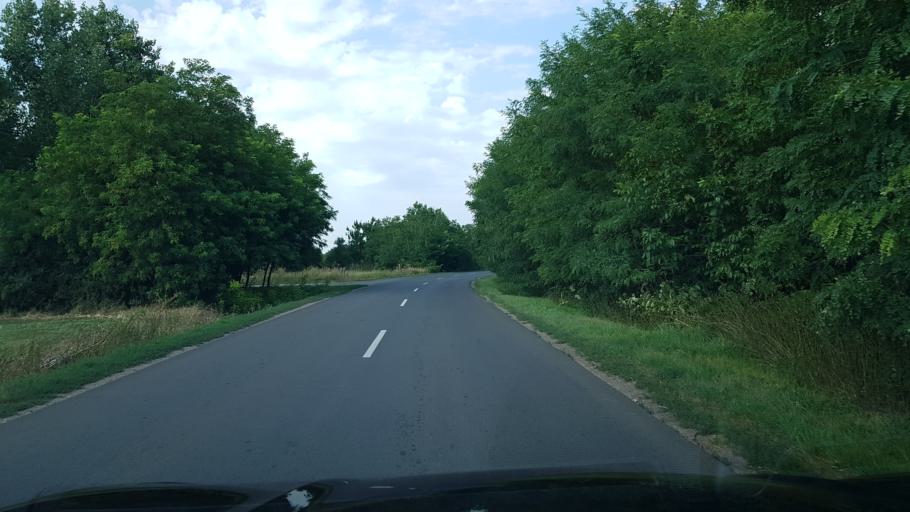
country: HU
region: Bekes
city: Fuzesgyarmat
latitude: 47.0817
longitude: 21.1963
